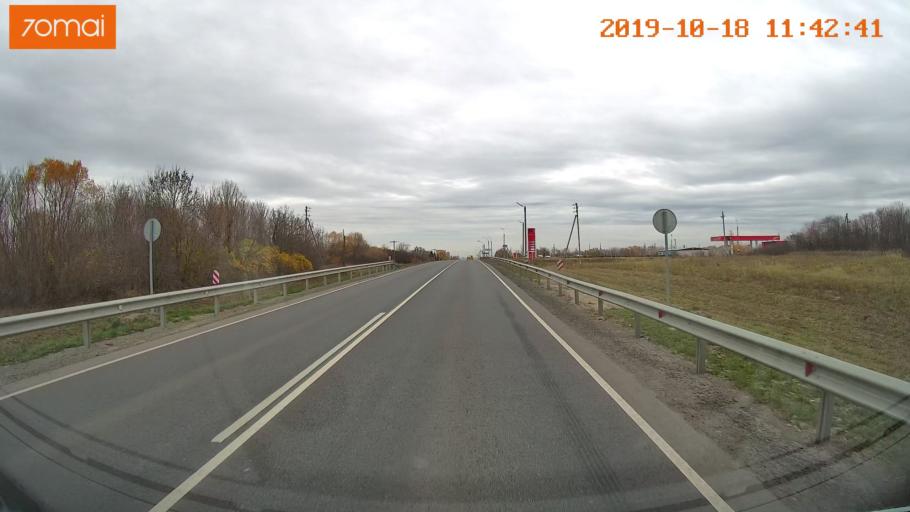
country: RU
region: Rjazan
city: Oktyabr'skiy
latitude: 54.1908
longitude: 38.9326
